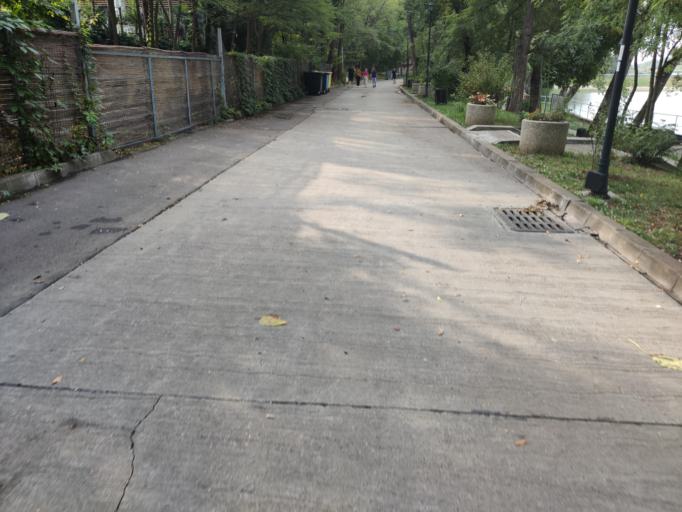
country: RO
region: Iasi
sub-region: Municipiul Iasi
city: Iasi
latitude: 47.1812
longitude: 27.6037
